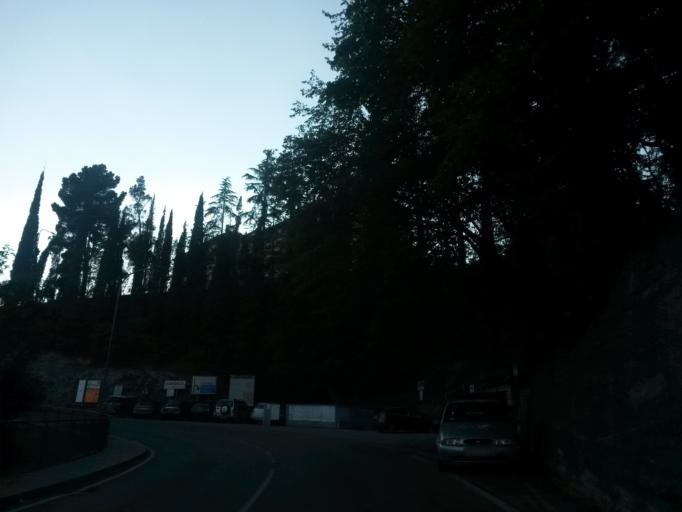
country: IT
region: Lombardy
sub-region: Provincia di Brescia
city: Gardola
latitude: 45.7385
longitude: 10.7242
